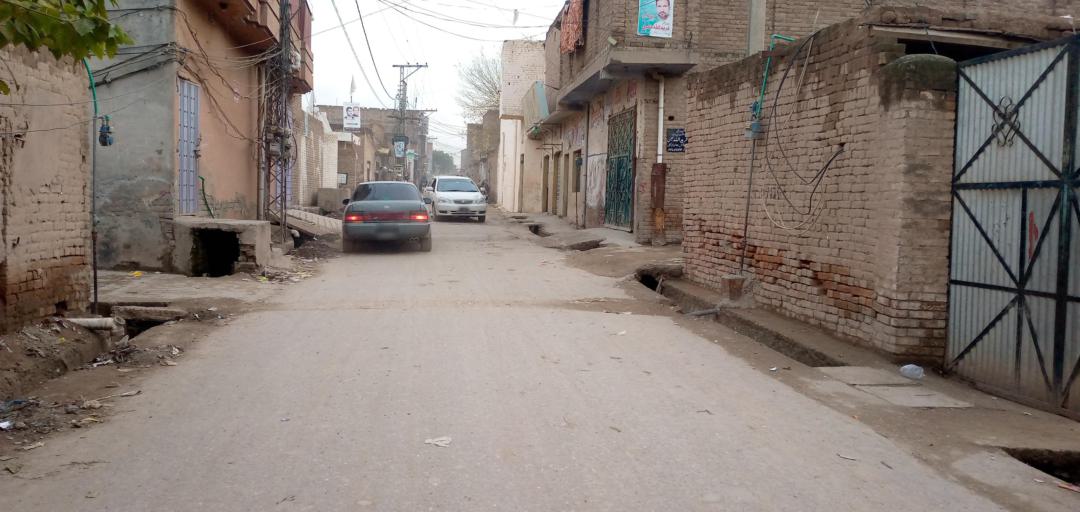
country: PK
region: Khyber Pakhtunkhwa
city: Peshawar
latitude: 34.0155
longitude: 71.5008
